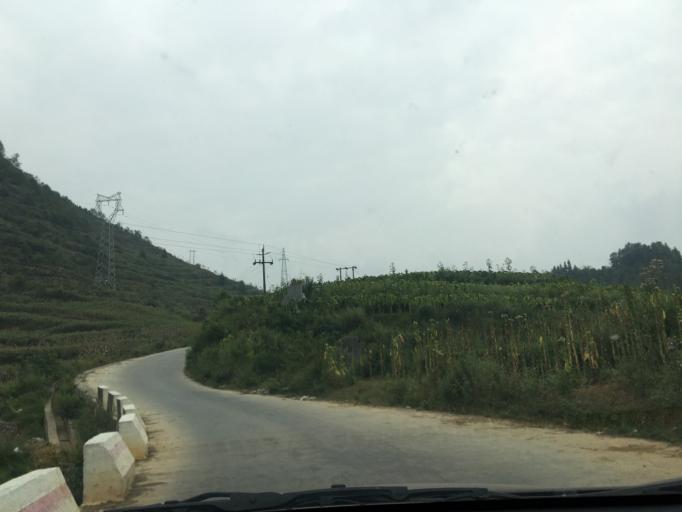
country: CN
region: Guangxi Zhuangzu Zizhiqu
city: Xinzhou
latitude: 25.5376
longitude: 105.6047
